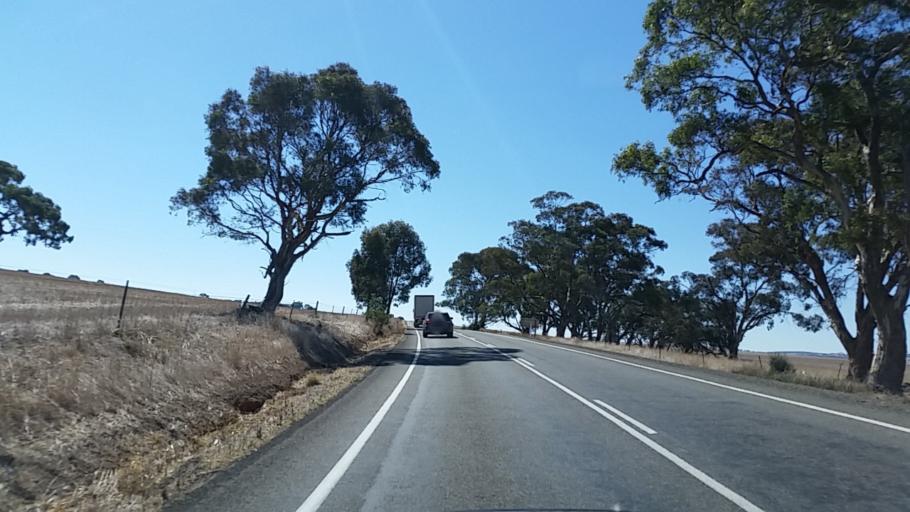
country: AU
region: South Australia
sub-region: Clare and Gilbert Valleys
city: Clare
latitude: -34.0388
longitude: 138.8013
